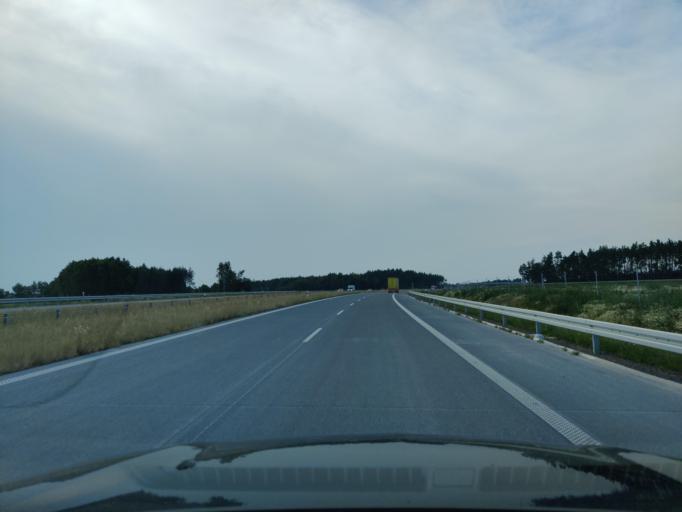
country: PL
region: Masovian Voivodeship
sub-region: Powiat mlawski
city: Strzegowo
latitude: 52.8860
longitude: 20.2654
